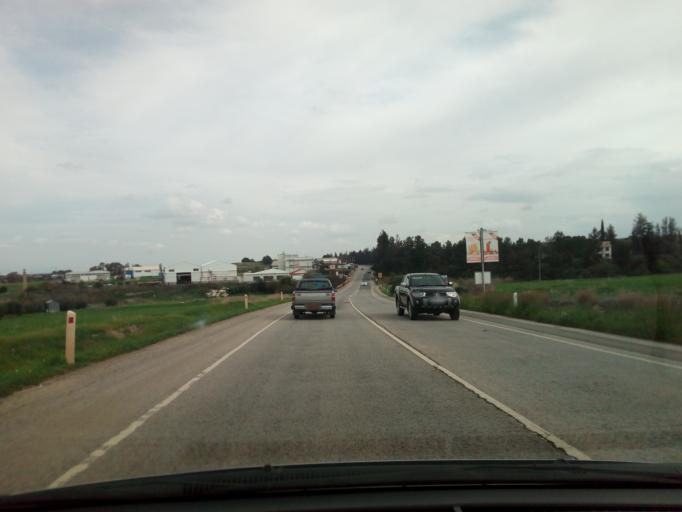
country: CY
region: Lefkosia
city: Akaki
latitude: 35.1358
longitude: 33.1118
